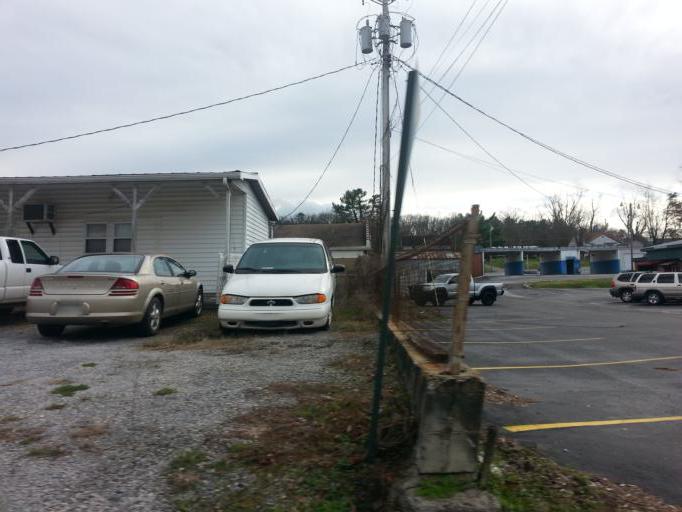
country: US
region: Tennessee
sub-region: Greene County
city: Greeneville
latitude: 36.1562
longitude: -82.8449
